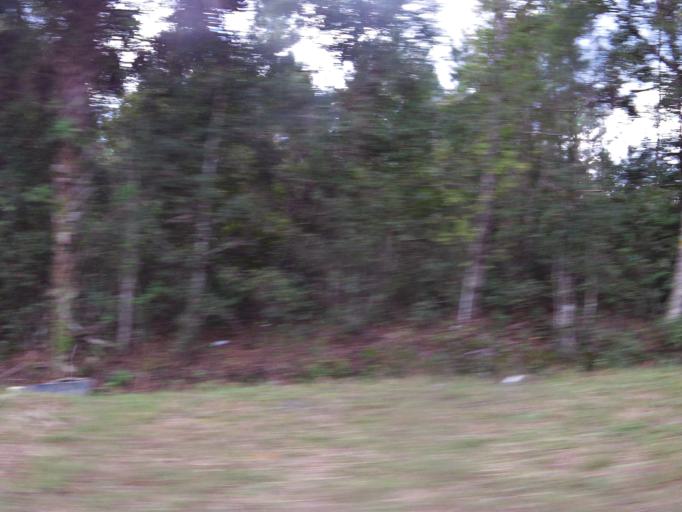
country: US
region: Florida
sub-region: Saint Johns County
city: Villano Beach
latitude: 29.9882
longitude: -81.4427
